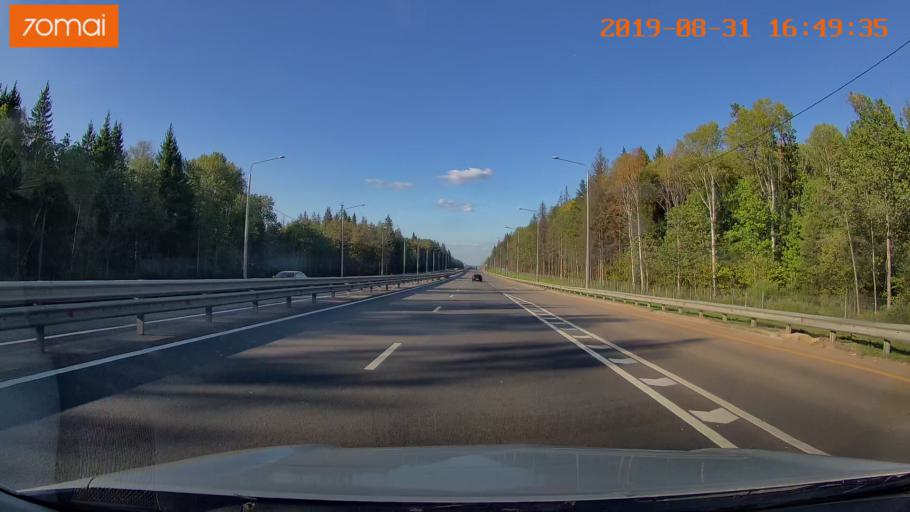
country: RU
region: Kaluga
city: Pyatovskiy
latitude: 54.6931
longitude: 36.1559
